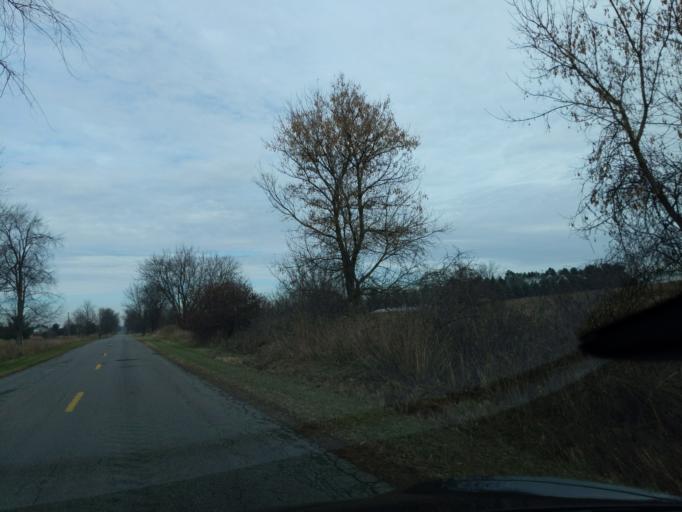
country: US
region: Michigan
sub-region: Ingham County
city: Leslie
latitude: 42.4998
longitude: -84.5024
